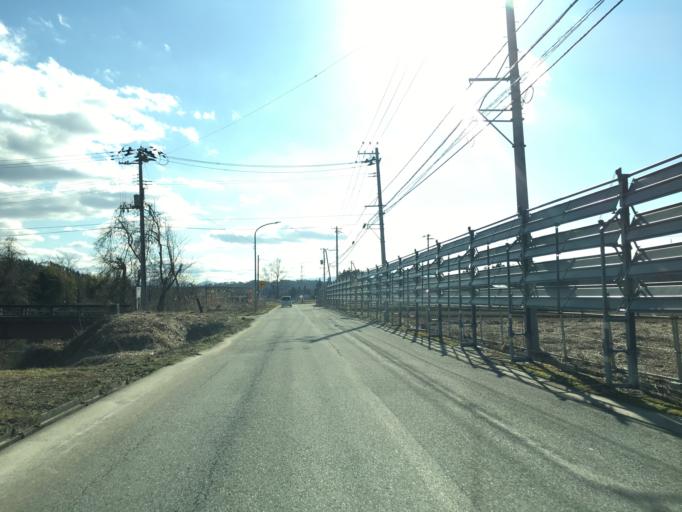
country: JP
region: Yamagata
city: Nagai
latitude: 38.0018
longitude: 140.0213
